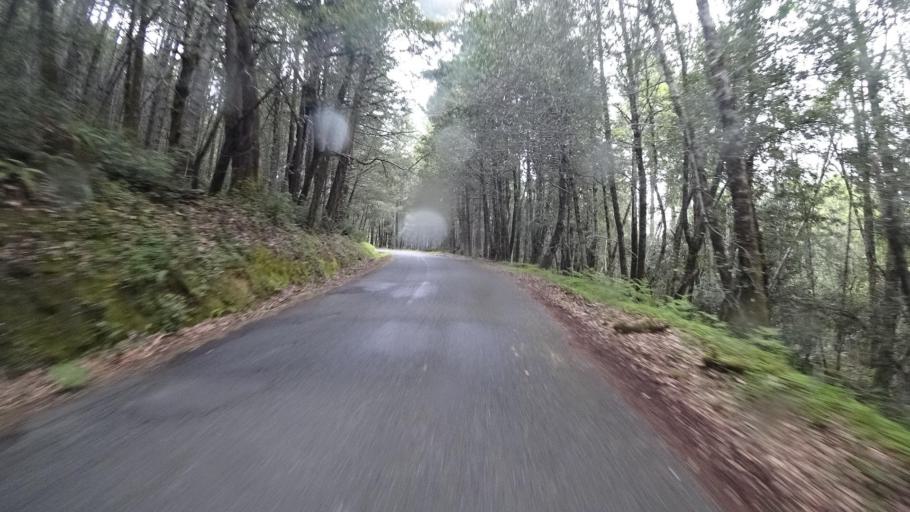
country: US
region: California
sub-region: Humboldt County
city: Willow Creek
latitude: 41.1990
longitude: -123.7705
